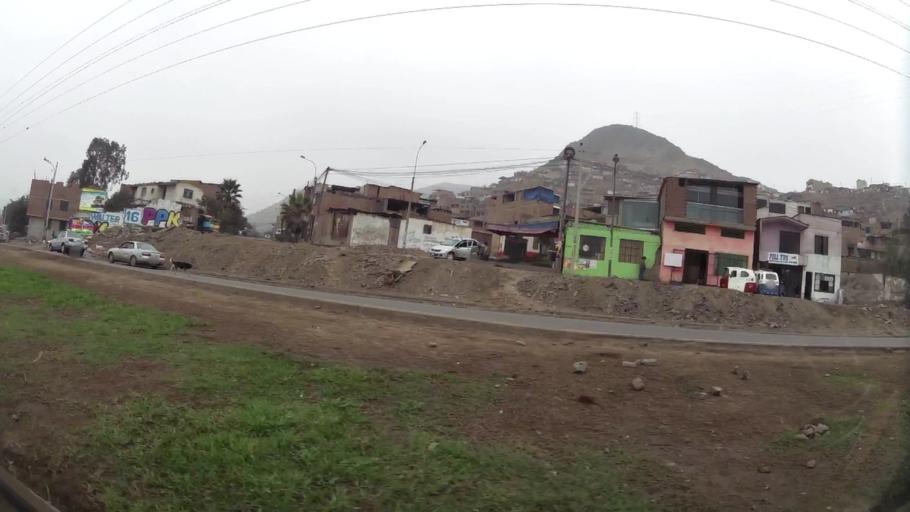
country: PE
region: Lima
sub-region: Lima
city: Surco
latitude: -12.1755
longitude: -76.9422
